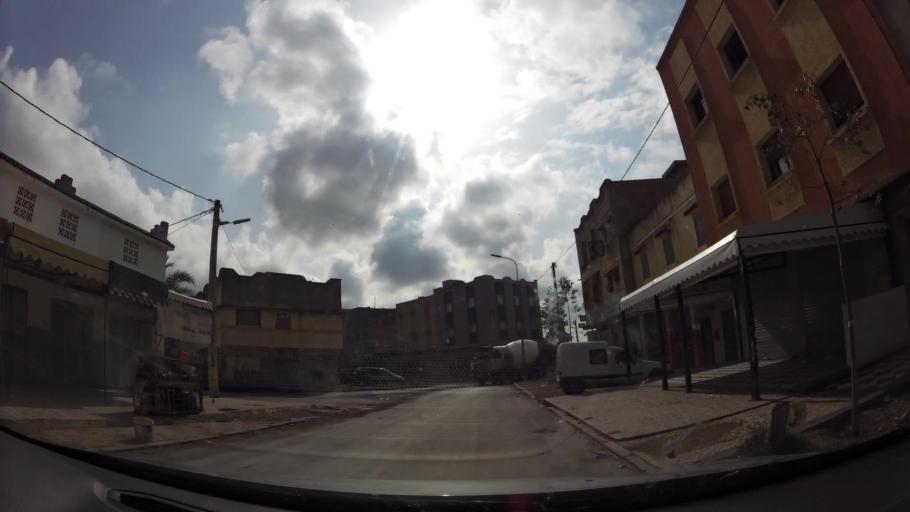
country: MA
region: Rabat-Sale-Zemmour-Zaer
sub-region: Khemisset
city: Tiflet
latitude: 33.8854
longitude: -6.3128
